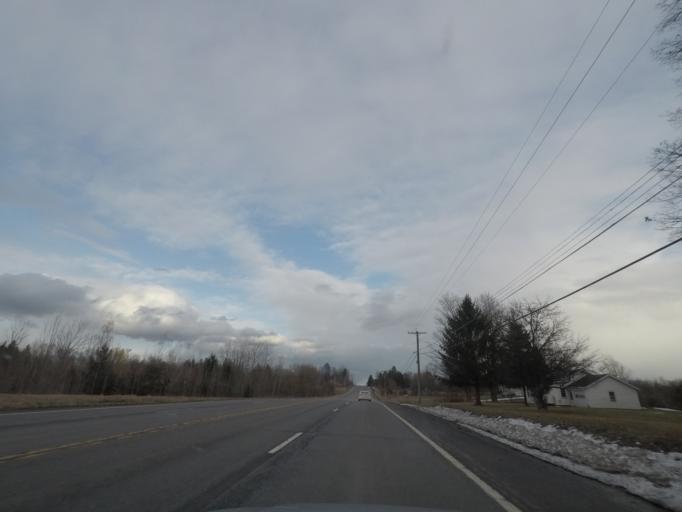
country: US
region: New York
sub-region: Oneida County
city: Clark Mills
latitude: 43.0804
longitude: -75.4125
